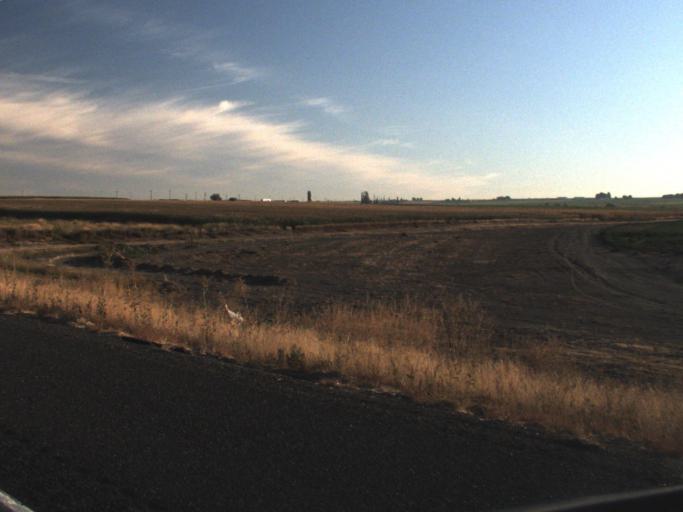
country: US
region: Washington
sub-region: Franklin County
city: Pasco
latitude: 46.3522
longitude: -119.0882
